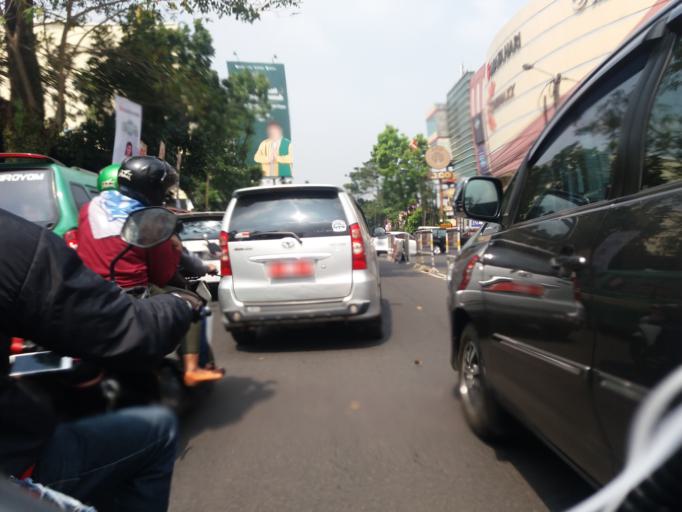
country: ID
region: West Java
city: Bandung
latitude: -6.9051
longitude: 107.5976
